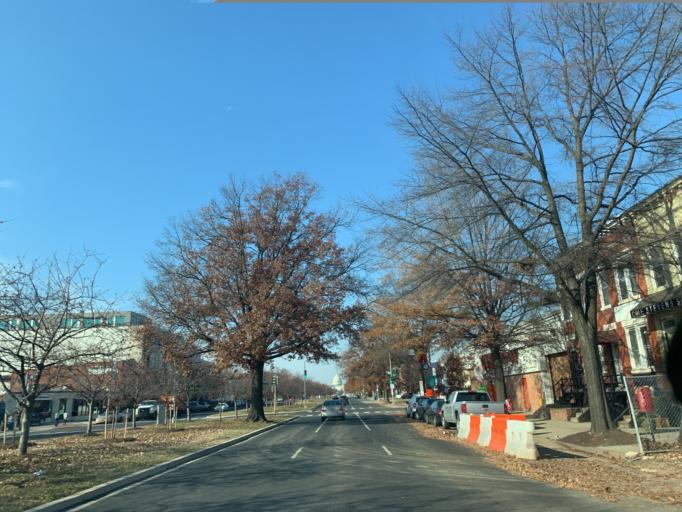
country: US
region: Washington, D.C.
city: Washington, D.C.
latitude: 38.8820
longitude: -76.9893
